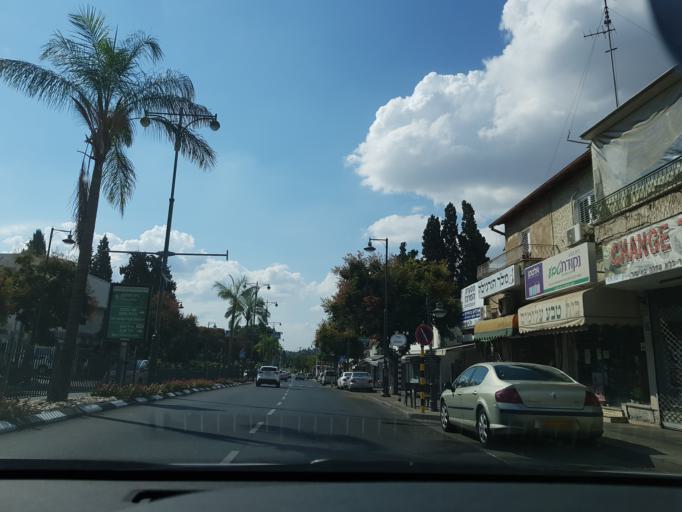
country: IL
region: Central District
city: Ness Ziona
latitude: 31.9277
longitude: 34.7981
